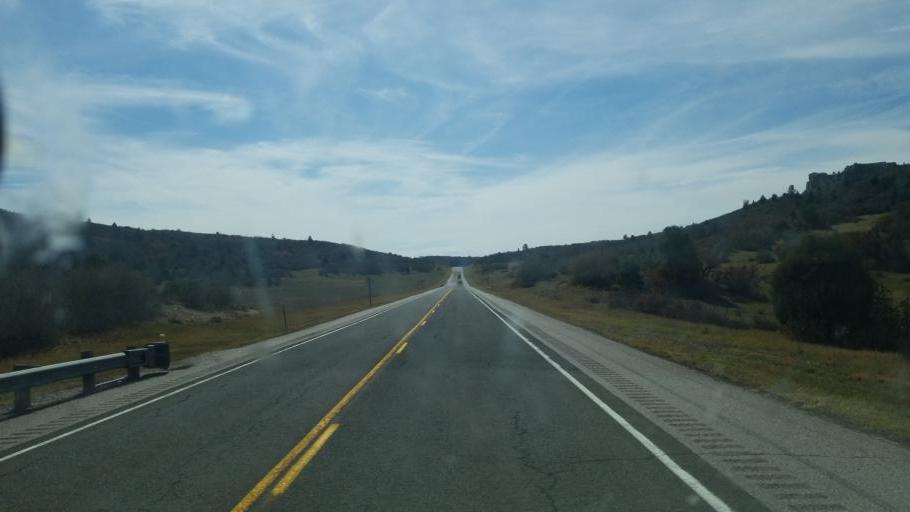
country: US
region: New Mexico
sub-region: Rio Arriba County
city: Chama
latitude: 36.9803
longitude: -106.7802
